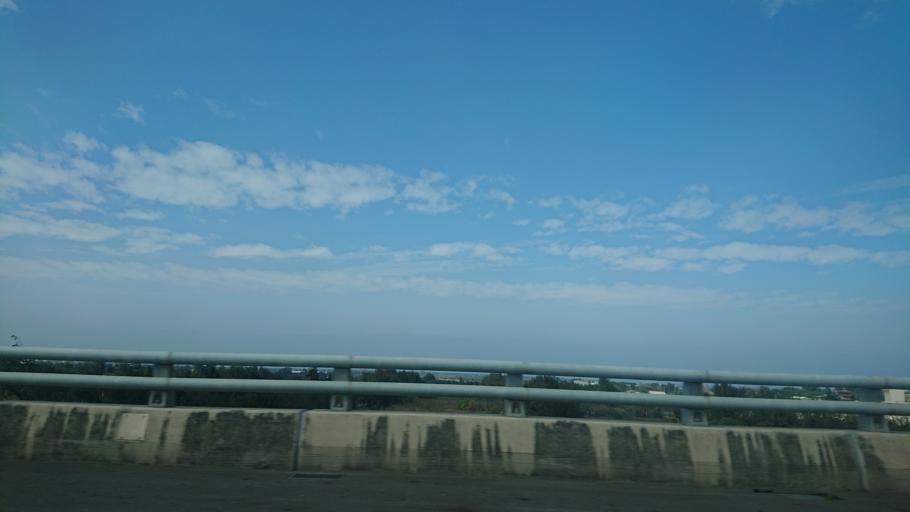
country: TW
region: Taiwan
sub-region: Yunlin
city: Douliu
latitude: 23.8524
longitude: 120.2956
